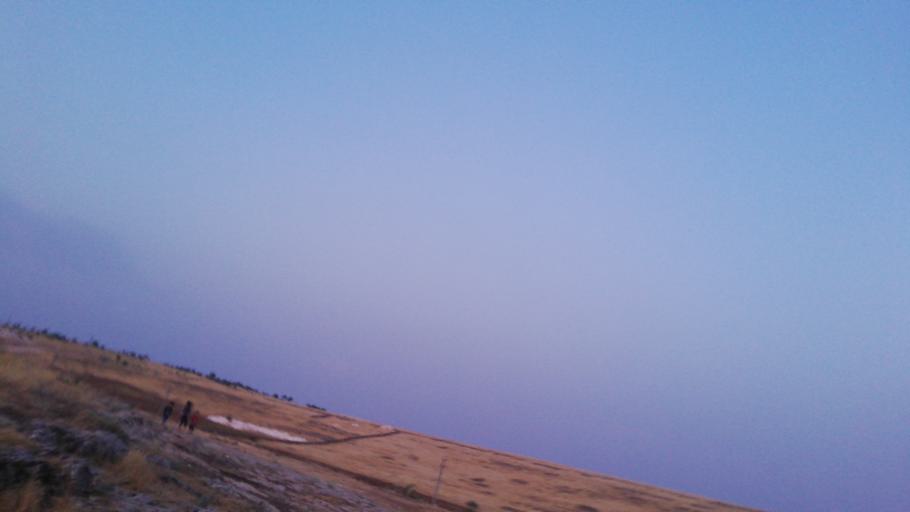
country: TR
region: Mardin
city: Kindirip
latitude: 37.4476
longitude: 41.2251
